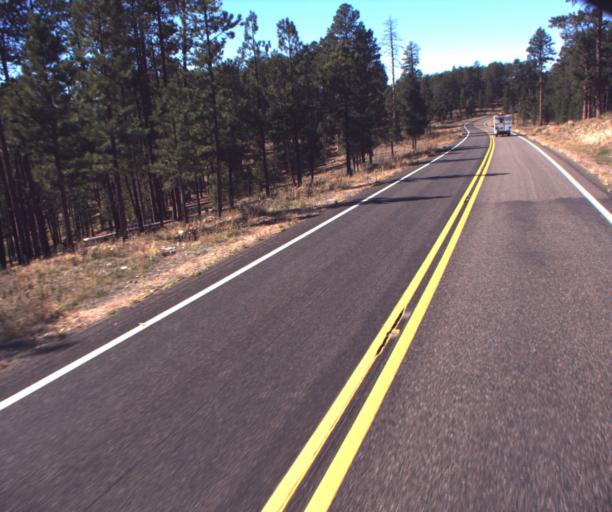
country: US
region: Arizona
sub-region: Coconino County
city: Fredonia
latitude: 36.6697
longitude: -112.2037
